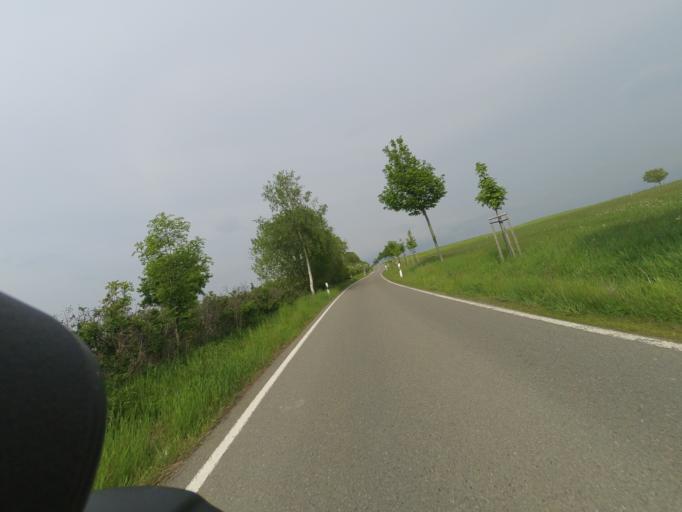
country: DE
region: Saxony
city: Pretzschendorf
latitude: 50.8573
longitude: 13.4746
